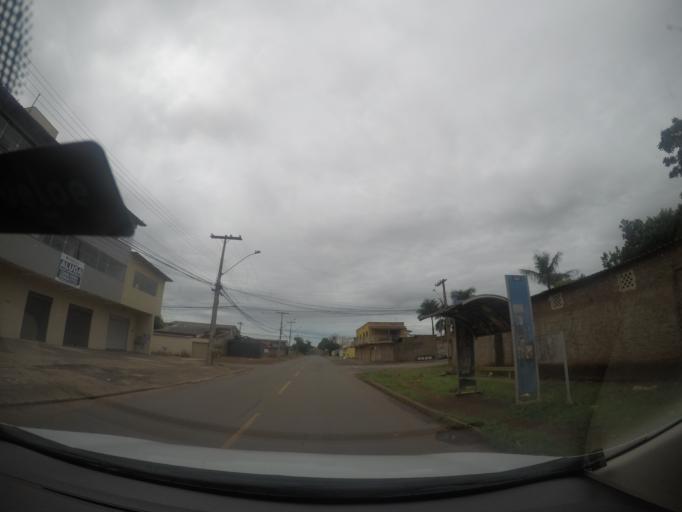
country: BR
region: Goias
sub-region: Goiania
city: Goiania
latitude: -16.7023
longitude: -49.3228
